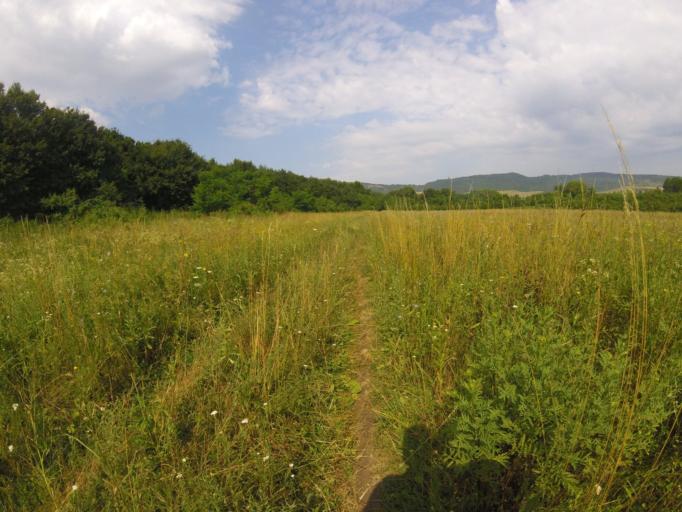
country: HU
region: Nograd
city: Matraverebely
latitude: 47.9674
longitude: 19.7827
